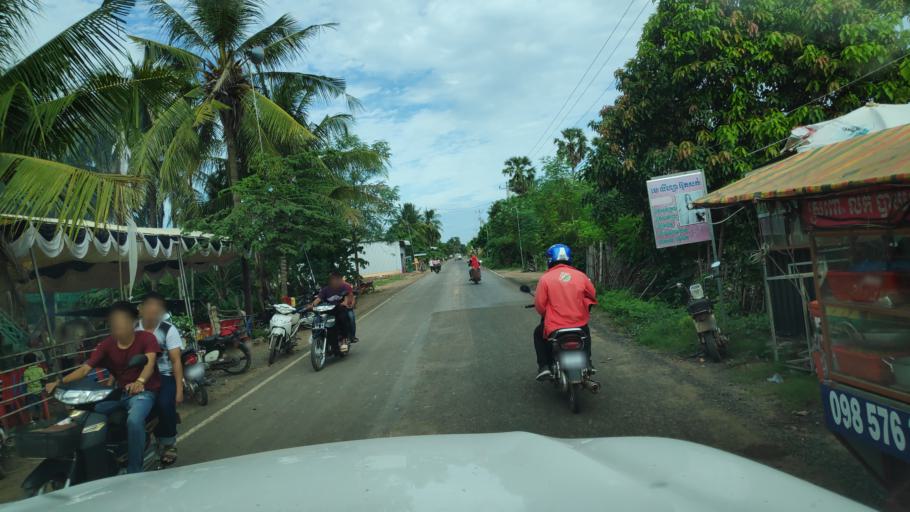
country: KH
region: Kampong Cham
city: Kampong Cham
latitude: 11.9465
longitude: 105.2515
